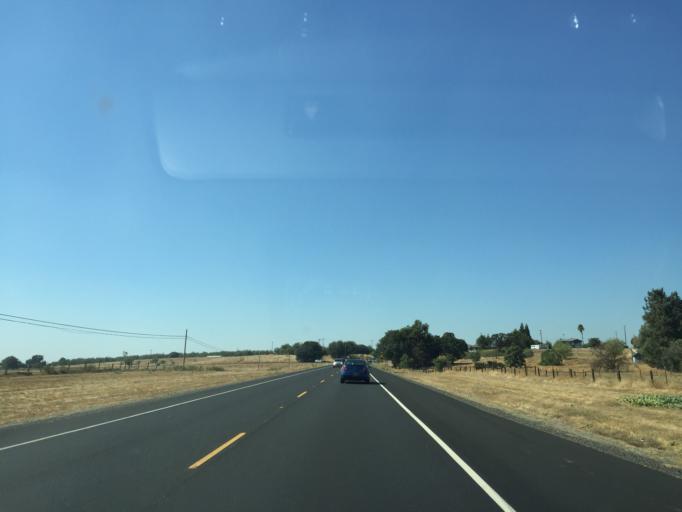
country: US
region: California
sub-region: Stanislaus County
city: East Oakdale
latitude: 37.7777
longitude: -120.7708
